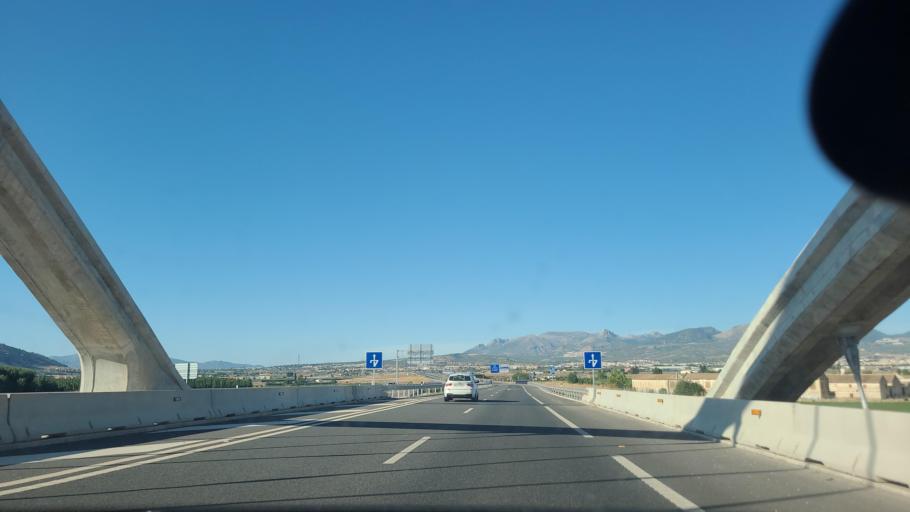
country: ES
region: Andalusia
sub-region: Provincia de Granada
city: Atarfe
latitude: 37.1948
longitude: -3.6859
